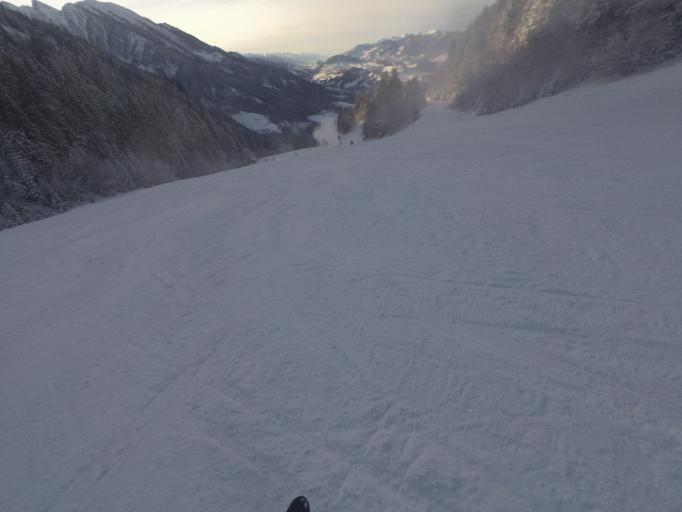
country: AT
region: Salzburg
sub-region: Politischer Bezirk Sankt Johann im Pongau
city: Sankt Johann im Pongau
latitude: 47.3173
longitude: 13.2155
